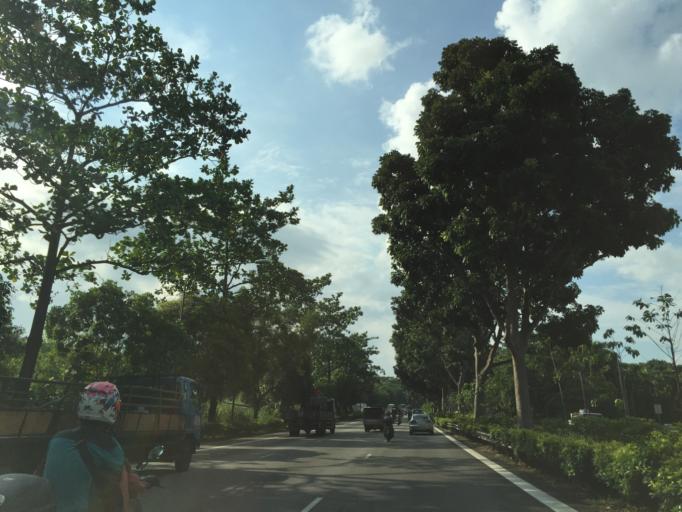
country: MY
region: Johor
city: Johor Bahru
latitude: 1.3906
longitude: 103.7744
